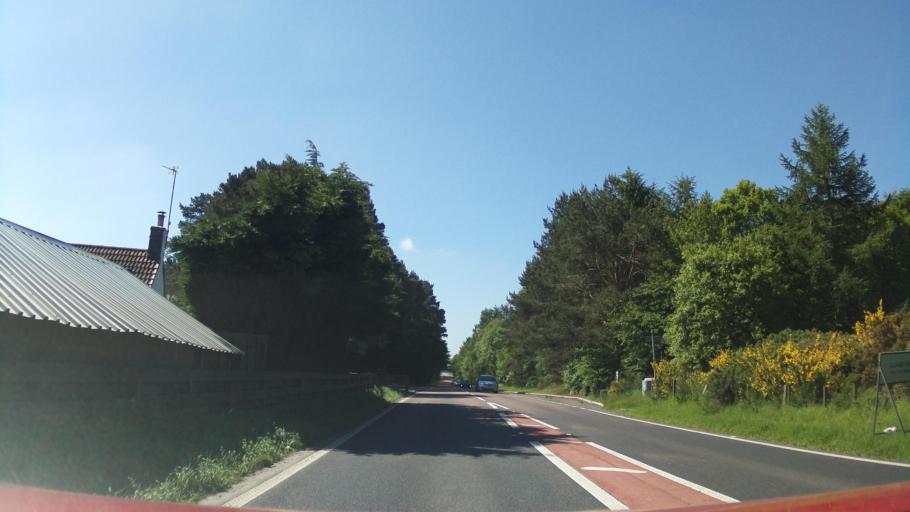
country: GB
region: Scotland
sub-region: Fife
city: Ladybank
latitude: 56.2788
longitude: -3.1348
